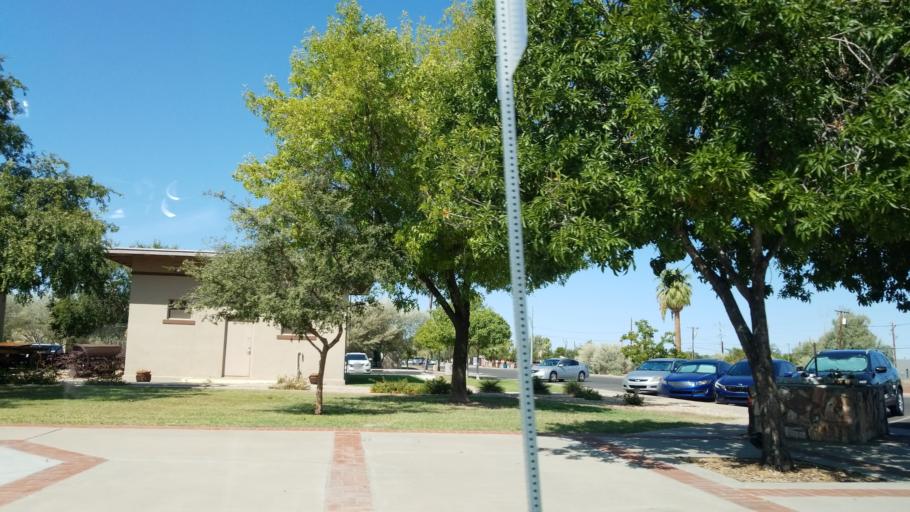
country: US
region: Arizona
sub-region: Maricopa County
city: Peoria
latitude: 33.5792
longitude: -112.2376
